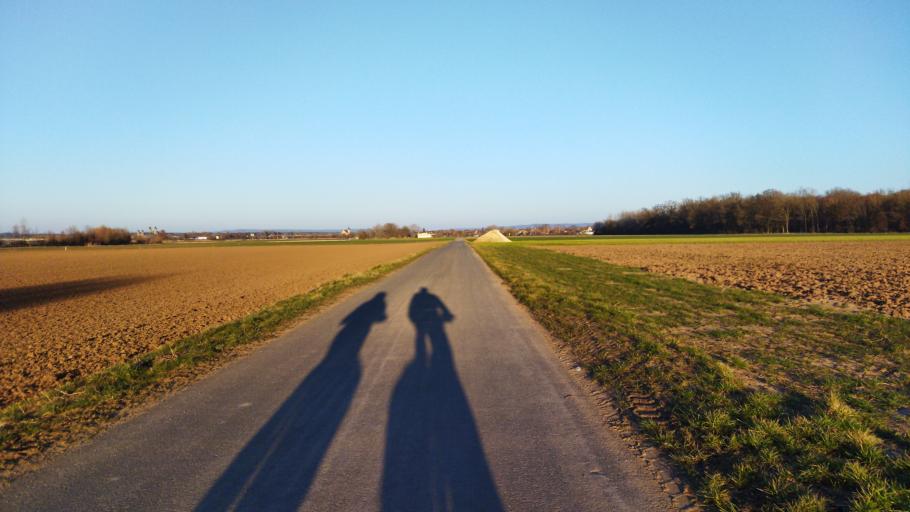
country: DE
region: Bavaria
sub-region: Regierungsbezirk Unterfranken
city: Dettelbach
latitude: 49.7891
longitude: 10.2022
